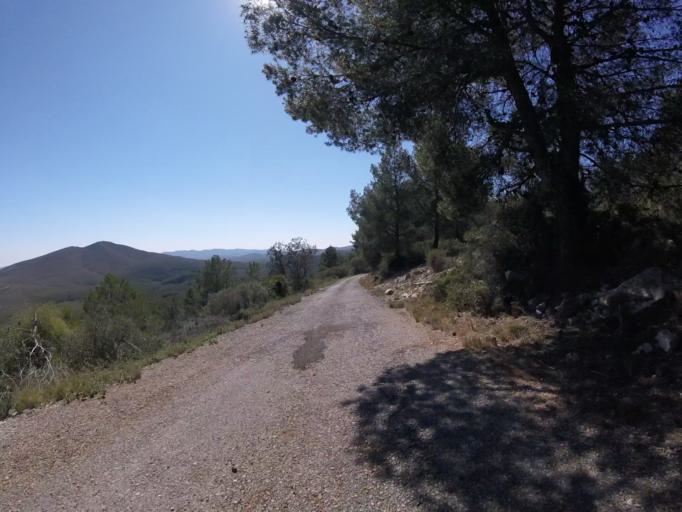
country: ES
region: Valencia
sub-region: Provincia de Castello
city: Cervera del Maestre
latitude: 40.4091
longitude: 0.1987
